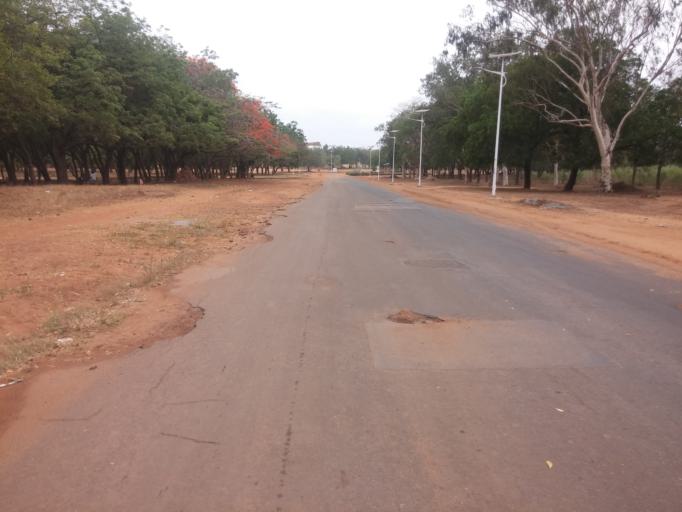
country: TG
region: Maritime
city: Lome
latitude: 6.1728
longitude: 1.2173
